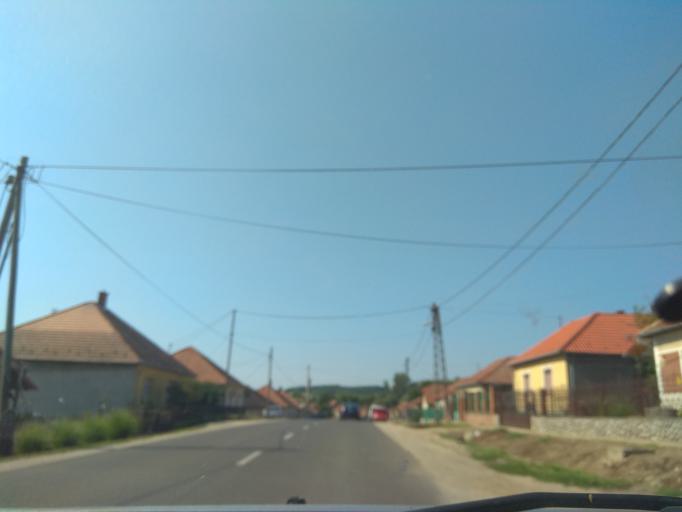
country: HU
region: Borsod-Abauj-Zemplen
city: Harsany
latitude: 47.9755
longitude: 20.7432
